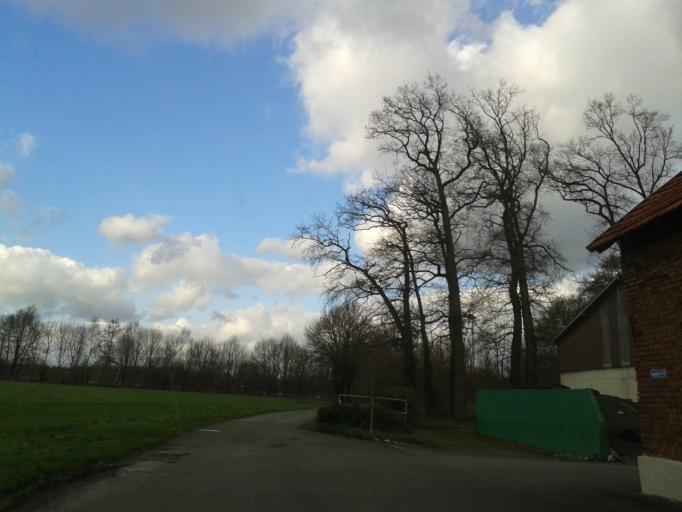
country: DE
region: North Rhine-Westphalia
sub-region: Regierungsbezirk Detmold
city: Hovelhof
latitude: 51.7406
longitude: 8.6397
